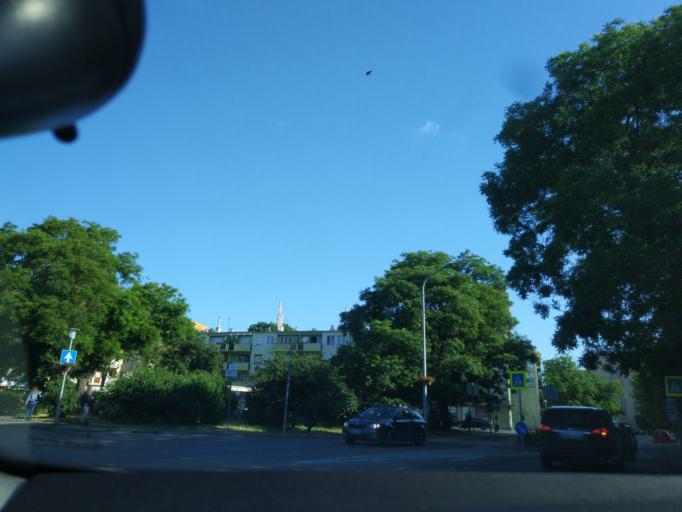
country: HU
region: Budapest
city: Budapest XX. keruelet
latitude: 47.4653
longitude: 19.1154
